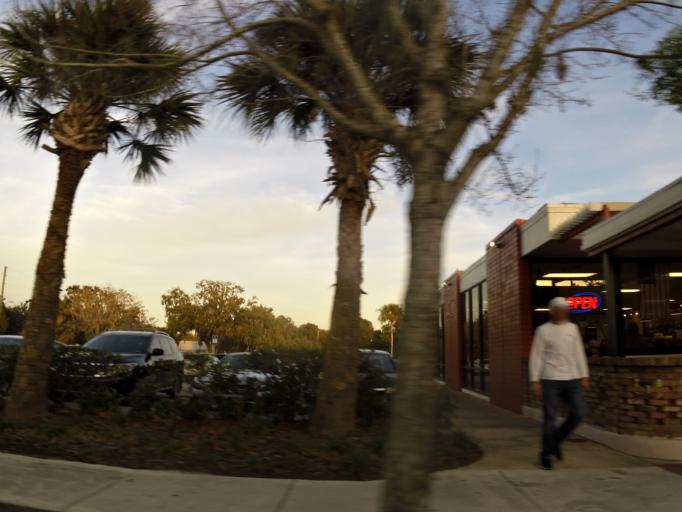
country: US
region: Florida
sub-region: Volusia County
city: DeLand
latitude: 29.0304
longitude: -81.3034
